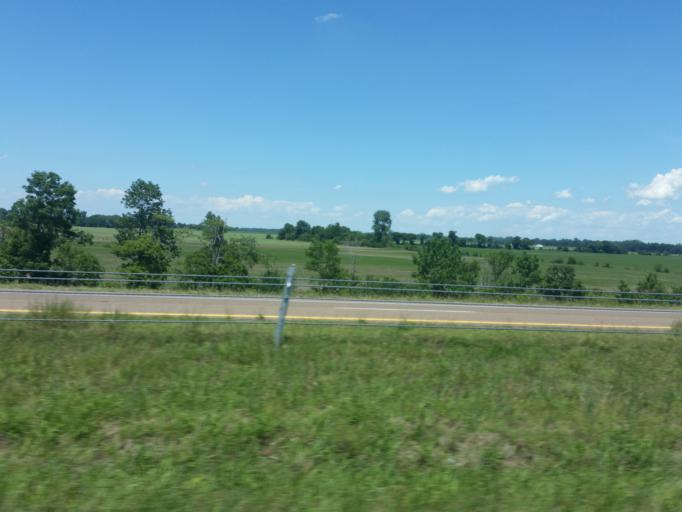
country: US
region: Missouri
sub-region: Pemiscot County
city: Caruthersville
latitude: 36.0959
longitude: -89.5984
